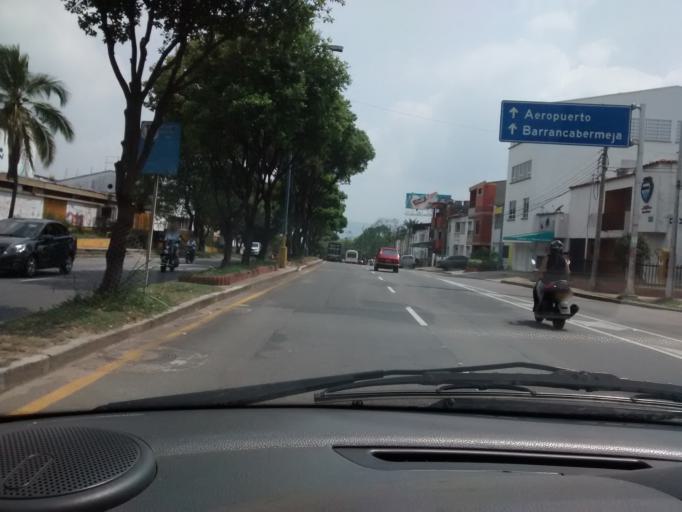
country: CO
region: Santander
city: Bucaramanga
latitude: 7.1039
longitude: -73.1136
